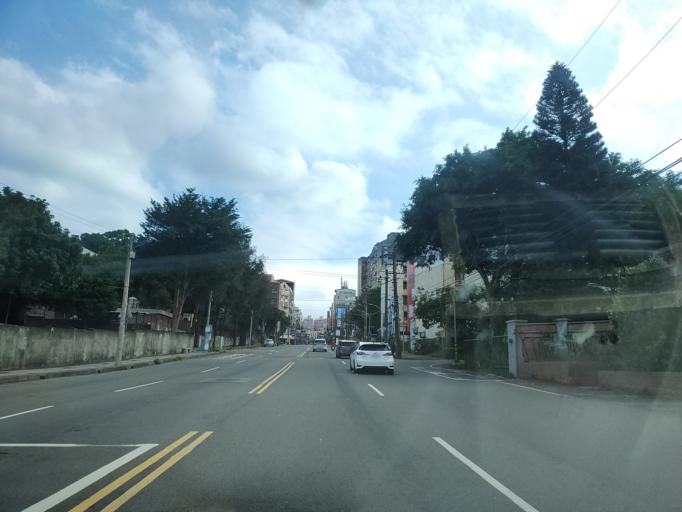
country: TW
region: Taiwan
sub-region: Hsinchu
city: Hsinchu
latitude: 24.8004
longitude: 120.9972
